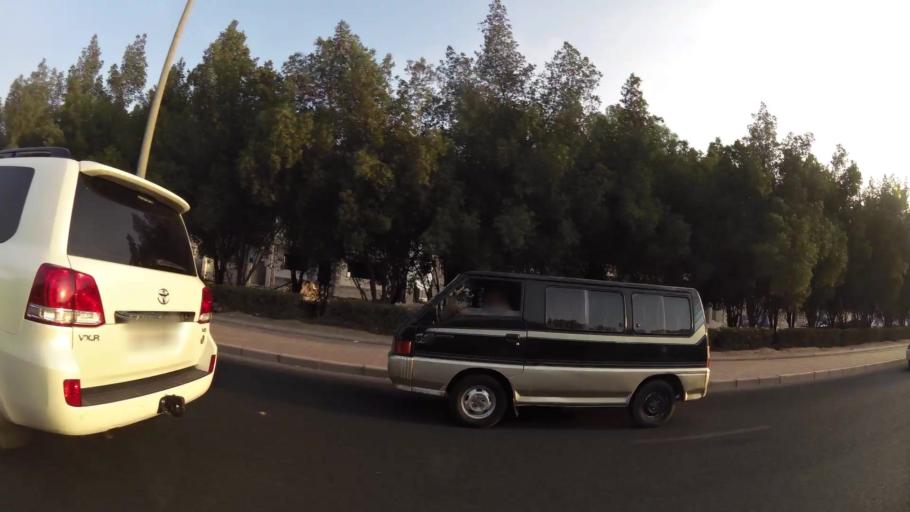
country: KW
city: Al Funaytis
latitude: 29.2469
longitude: 48.0853
